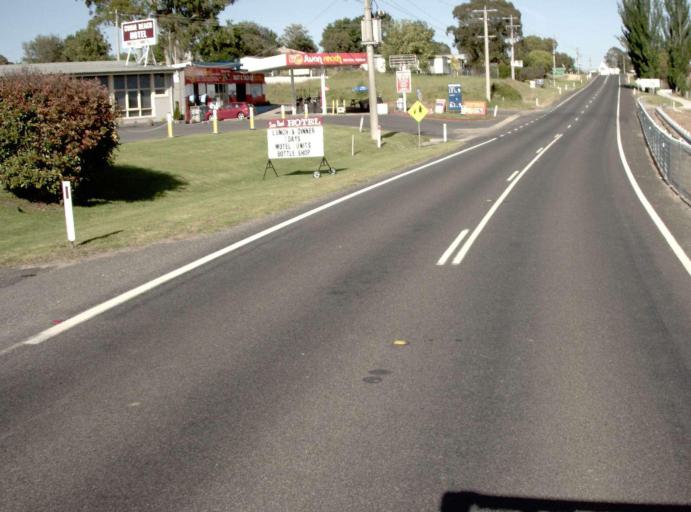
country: AU
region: Victoria
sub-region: East Gippsland
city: Lakes Entrance
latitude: -37.8225
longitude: 147.8608
